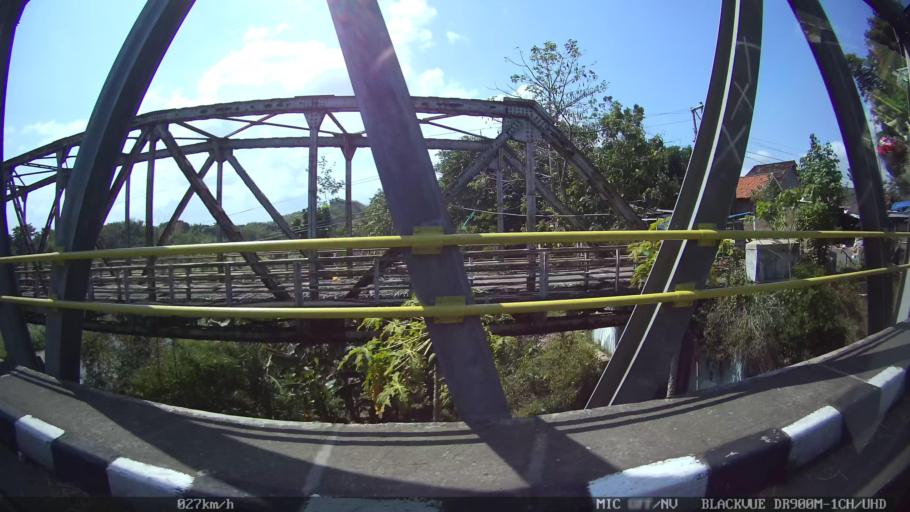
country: ID
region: Daerah Istimewa Yogyakarta
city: Pundong
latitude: -7.9519
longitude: 110.3798
